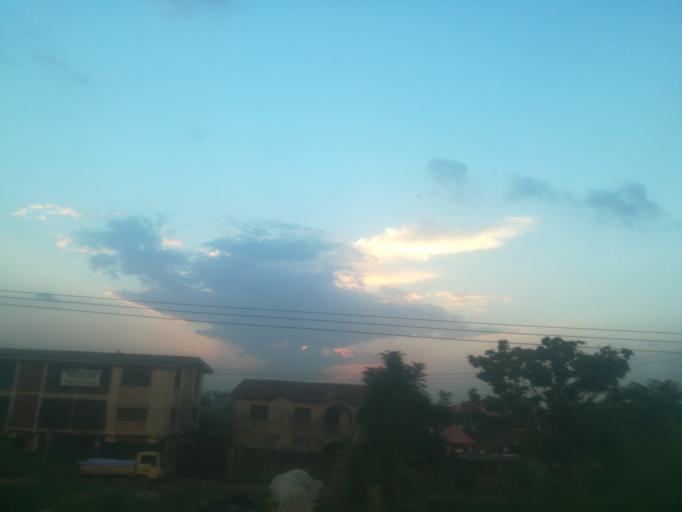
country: NG
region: Oyo
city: Ibadan
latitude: 7.4270
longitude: 3.9348
